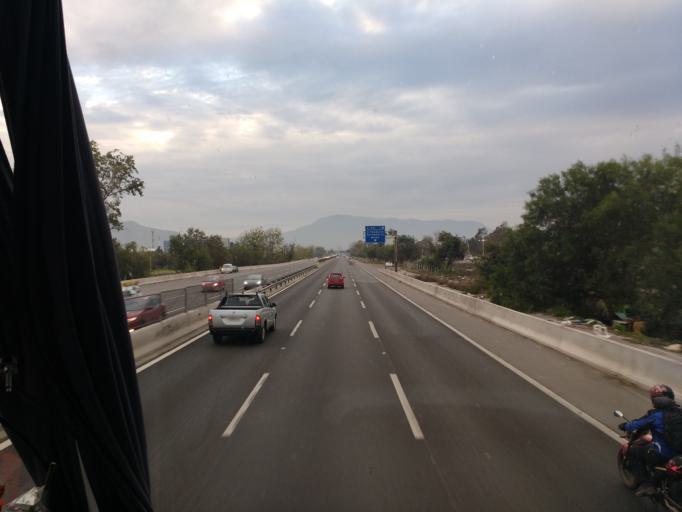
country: CL
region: Santiago Metropolitan
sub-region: Provincia de Santiago
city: Lo Prado
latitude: -33.4490
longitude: -70.7619
